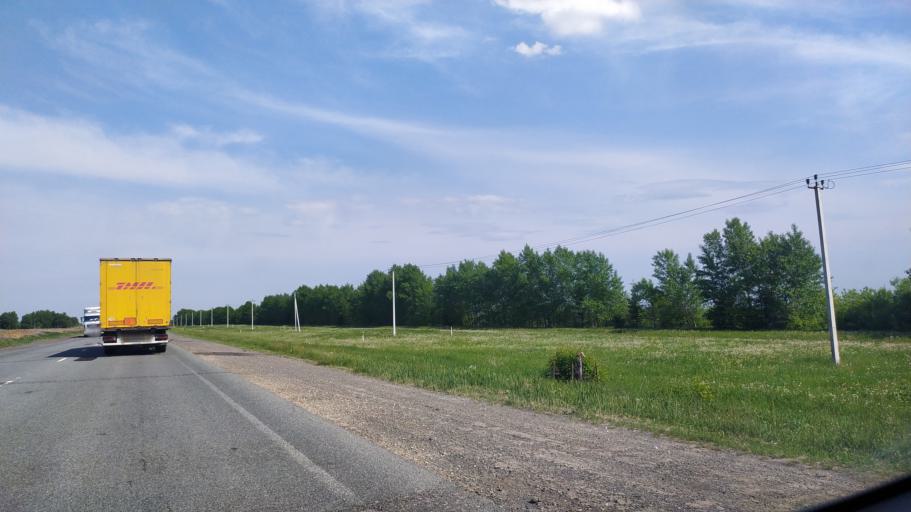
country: RU
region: Chuvashia
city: Kozlovka
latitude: 55.7297
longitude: 48.3149
